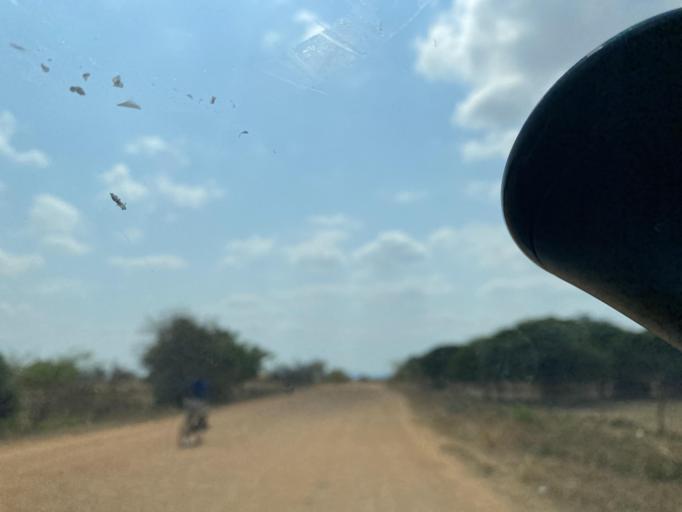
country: ZM
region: Lusaka
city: Chongwe
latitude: -15.5895
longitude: 28.7747
